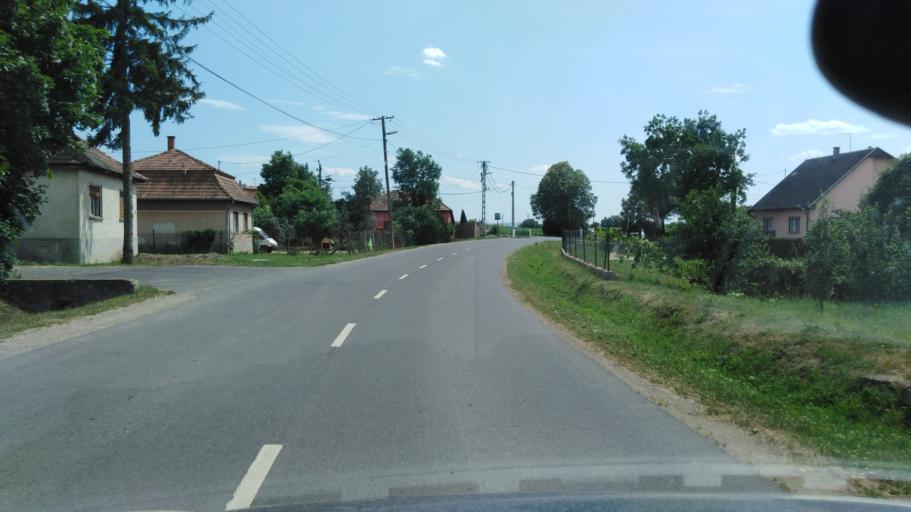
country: HU
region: Nograd
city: Szecseny
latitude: 48.1809
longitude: 19.5256
